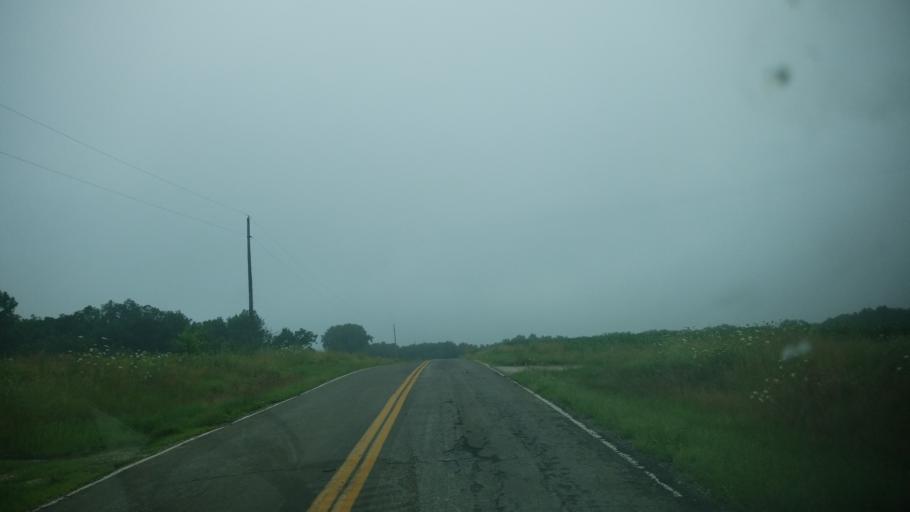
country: US
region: Missouri
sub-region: Audrain County
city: Vandalia
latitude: 39.2837
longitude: -91.3462
